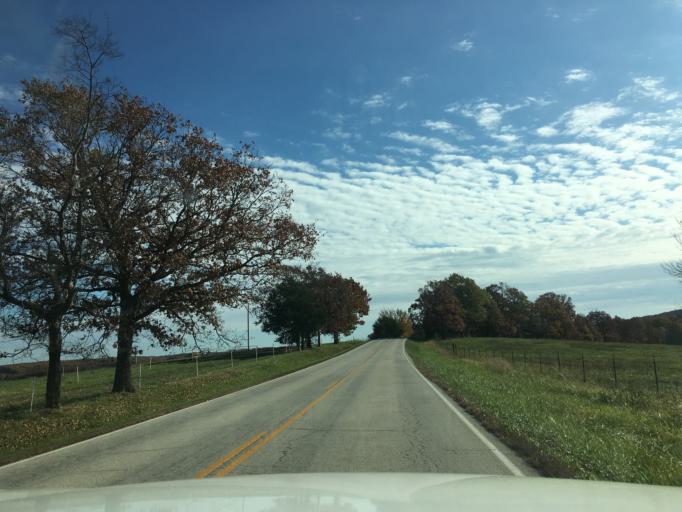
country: US
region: Missouri
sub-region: Maries County
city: Belle
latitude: 38.3482
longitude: -91.7955
